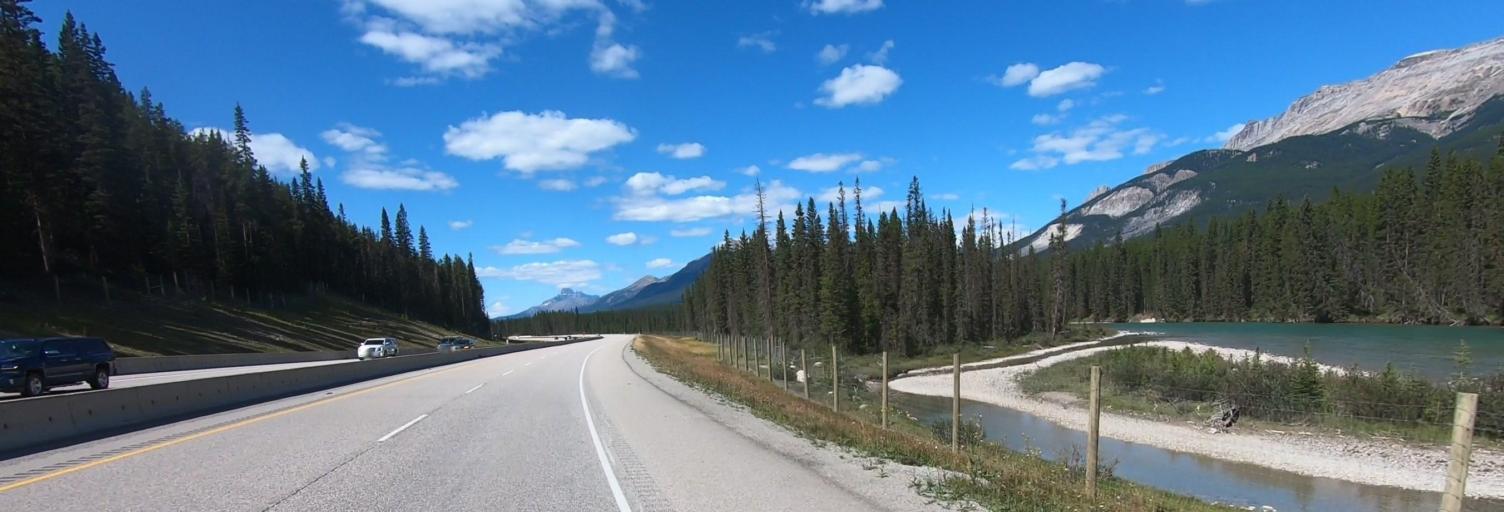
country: CA
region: Alberta
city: Lake Louise
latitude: 51.3297
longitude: -116.0534
